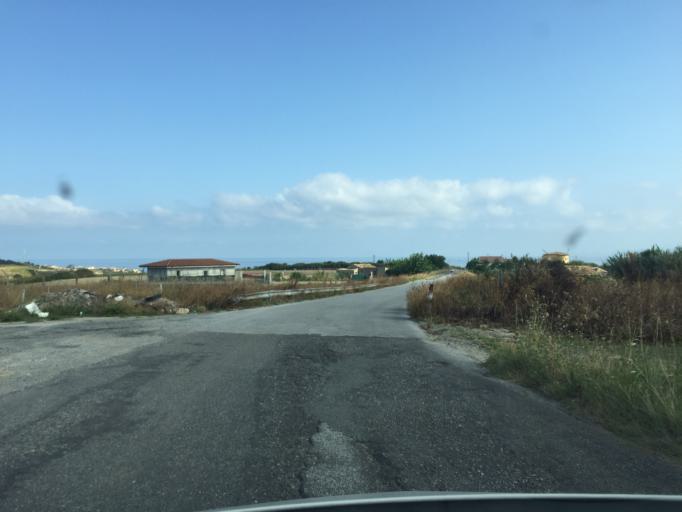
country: IT
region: Calabria
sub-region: Provincia di Vibo-Valentia
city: Pannaconi
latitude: 38.7101
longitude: 16.0492
